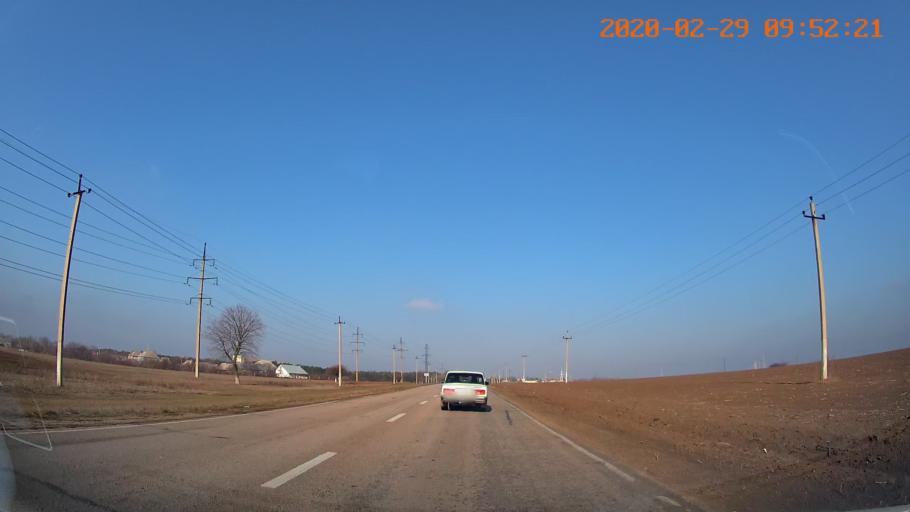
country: MD
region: Telenesti
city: Slobozia
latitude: 46.7154
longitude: 29.7315
